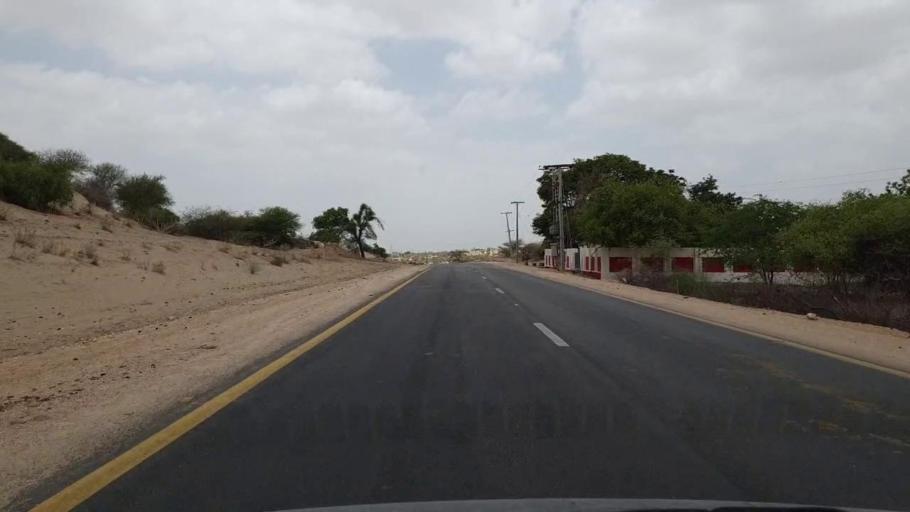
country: PK
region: Sindh
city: Naukot
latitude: 24.8445
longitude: 69.5472
